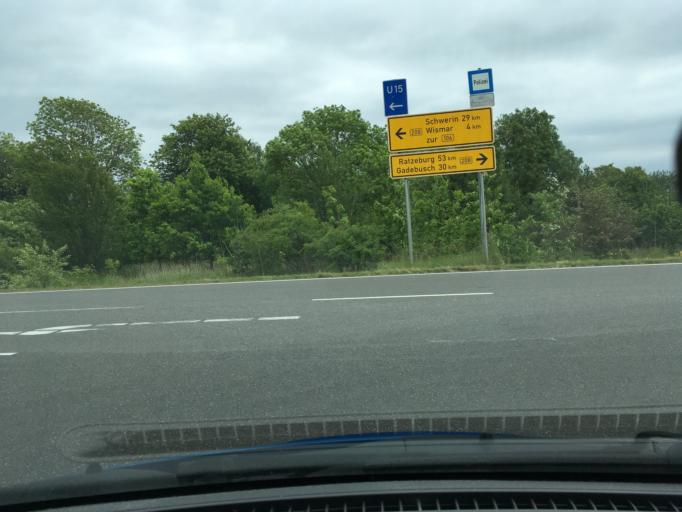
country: DE
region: Mecklenburg-Vorpommern
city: Mecklenburg
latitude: 53.8613
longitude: 11.4394
